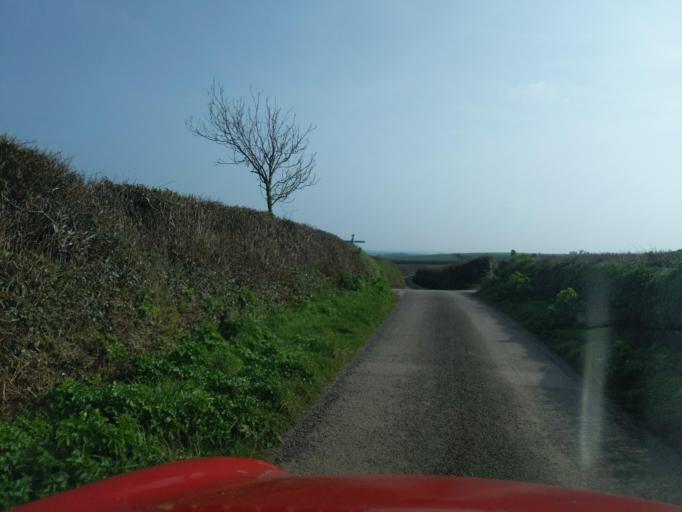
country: GB
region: England
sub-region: Devon
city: Kingsbridge
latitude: 50.2904
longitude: -3.7350
